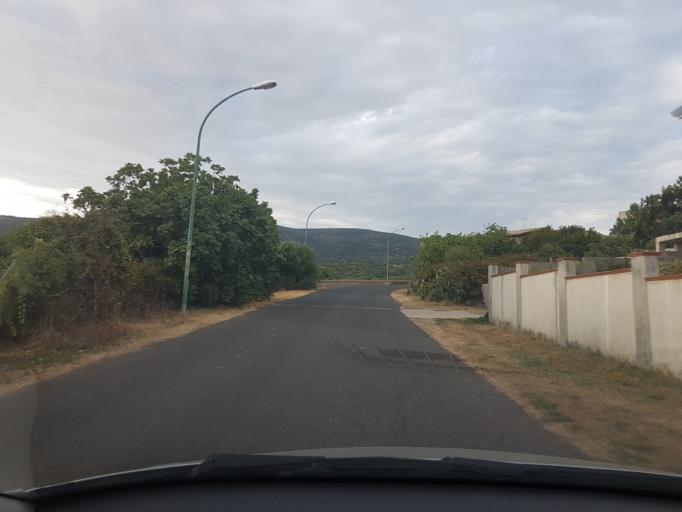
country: IT
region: Sardinia
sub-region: Provincia di Oristano
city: Seneghe
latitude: 40.0812
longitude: 8.6067
